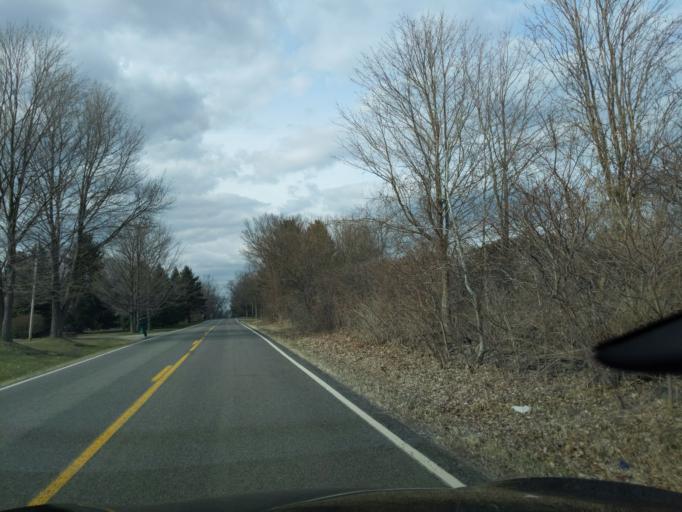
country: US
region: Michigan
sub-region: Ingham County
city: Mason
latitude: 42.5261
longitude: -84.4830
